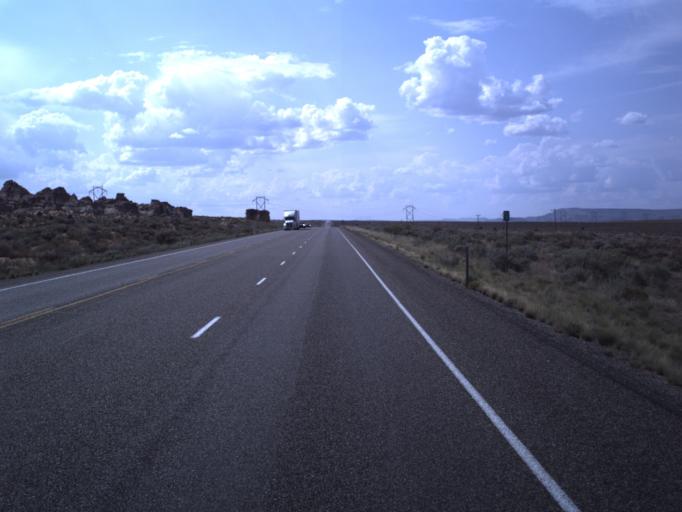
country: US
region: Arizona
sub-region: Coconino County
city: Page
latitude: 37.0864
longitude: -111.6906
